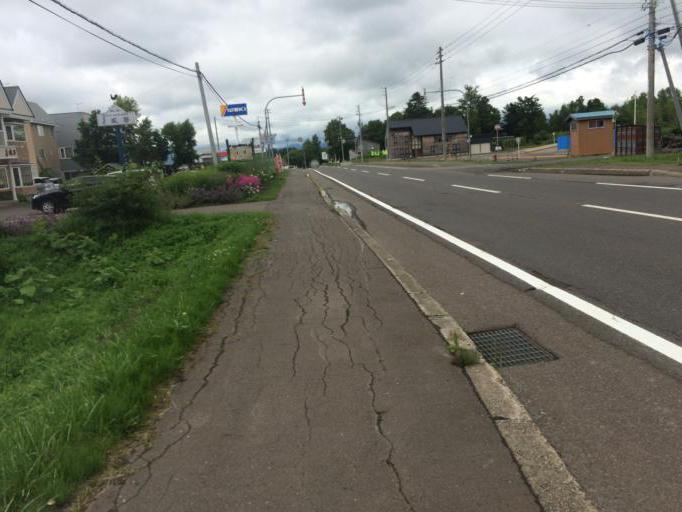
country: JP
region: Hokkaido
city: Niseko Town
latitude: 42.8715
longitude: 140.7492
